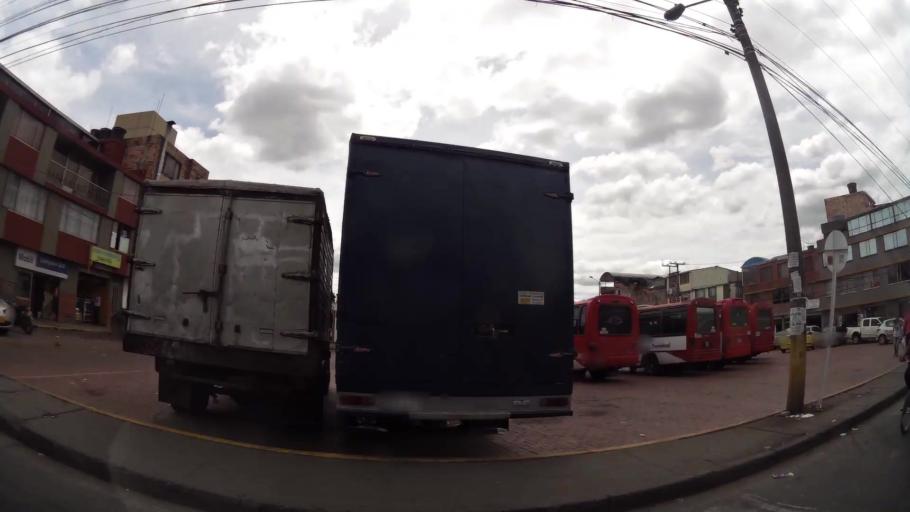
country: CO
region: Cundinamarca
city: Funza
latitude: 4.7140
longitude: -74.1265
